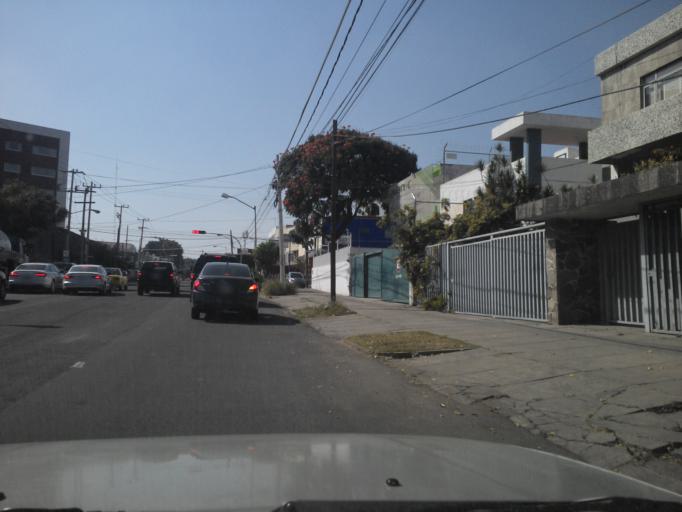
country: MX
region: Jalisco
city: Guadalajara
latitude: 20.6723
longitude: -103.3842
